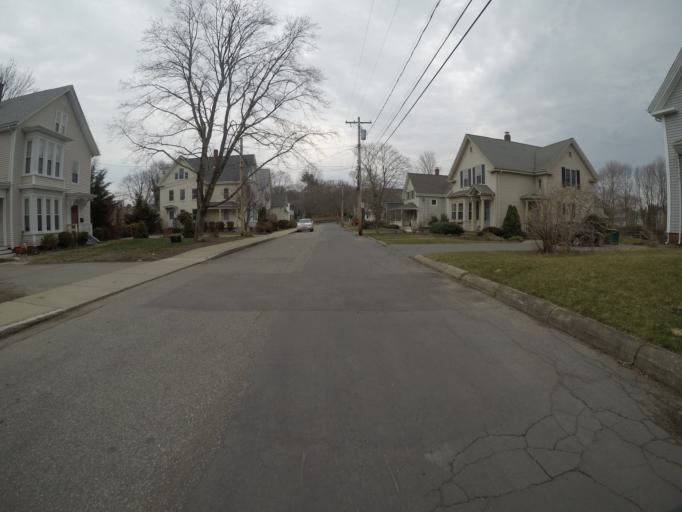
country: US
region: Massachusetts
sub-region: Bristol County
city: Easton
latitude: 42.0647
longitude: -71.0982
